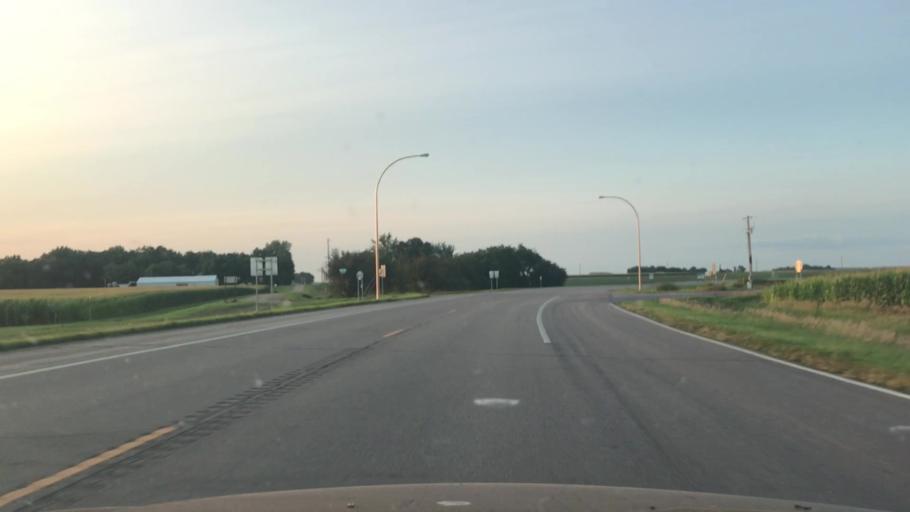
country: US
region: Minnesota
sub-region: Redwood County
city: Redwood Falls
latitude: 44.4122
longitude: -95.1274
